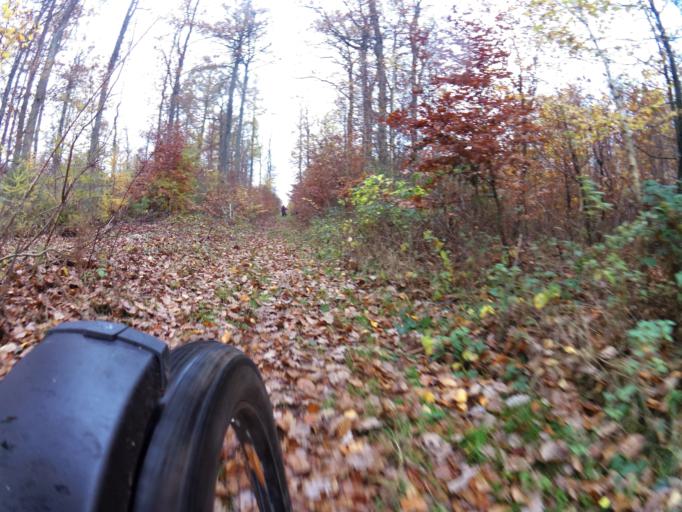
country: PL
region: Pomeranian Voivodeship
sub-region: Powiat pucki
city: Krokowa
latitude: 54.7316
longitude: 18.1319
